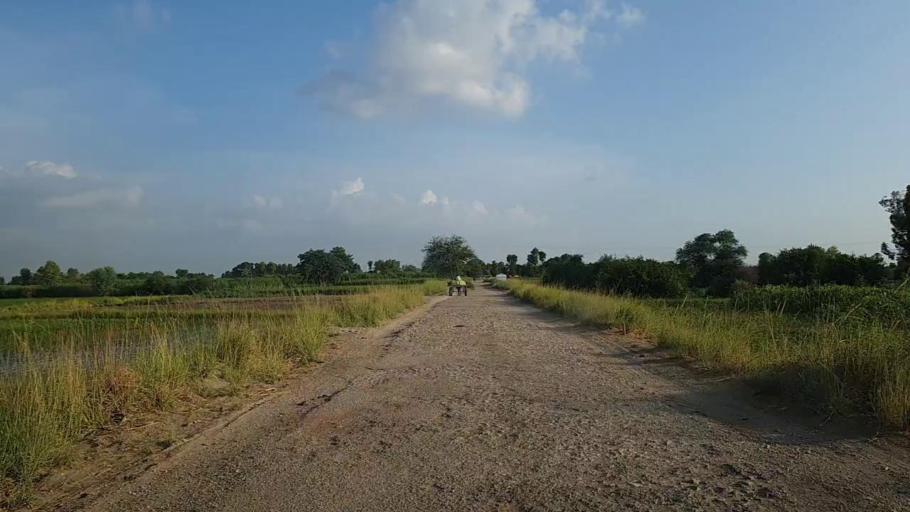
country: PK
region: Sindh
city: Hingorja
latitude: 27.0653
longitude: 68.4188
